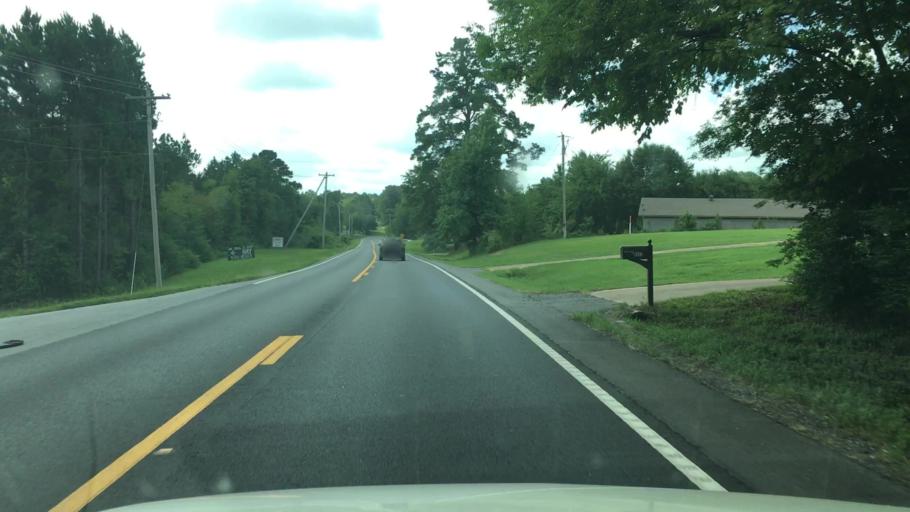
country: US
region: Arkansas
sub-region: Garland County
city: Lake Hamilton
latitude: 34.2985
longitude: -93.1639
